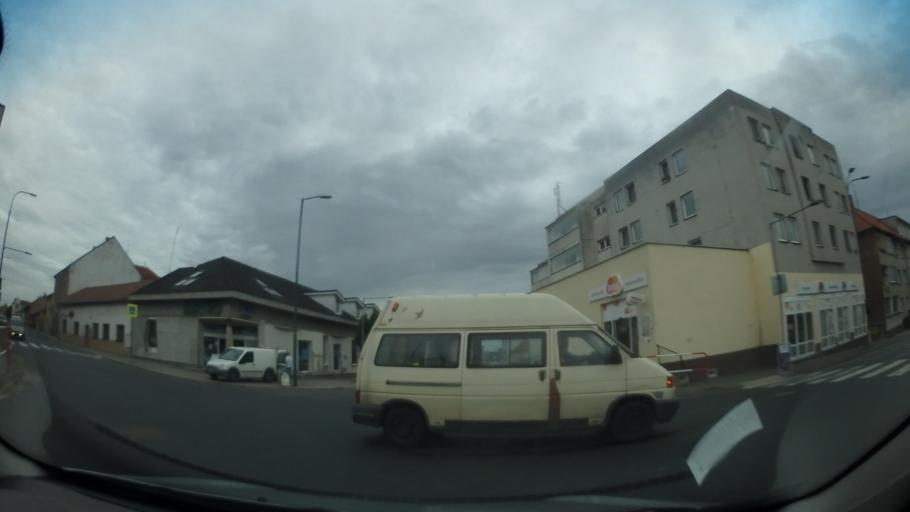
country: CZ
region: Central Bohemia
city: Lysa nad Labem
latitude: 50.2022
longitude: 14.8427
